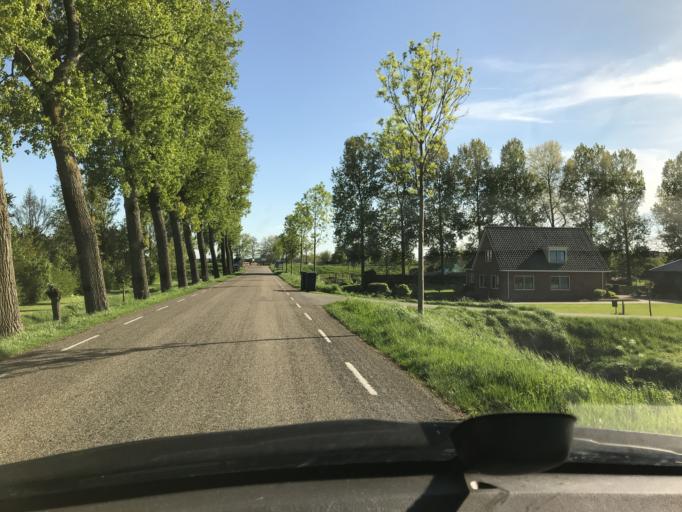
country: NL
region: Zeeland
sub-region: Gemeente Goes
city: Goes
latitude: 51.5566
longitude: 3.8103
